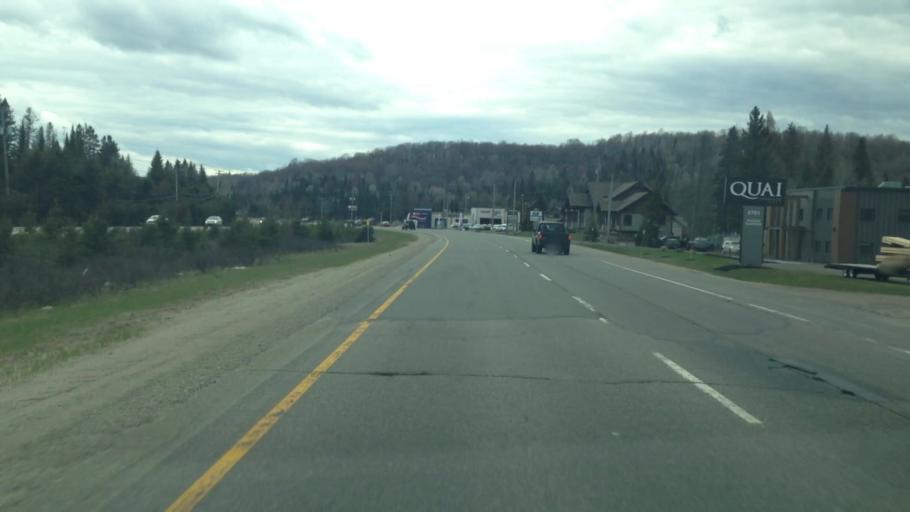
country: CA
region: Quebec
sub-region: Laurentides
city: Sainte-Agathe-des-Monts
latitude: 46.0749
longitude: -74.3153
